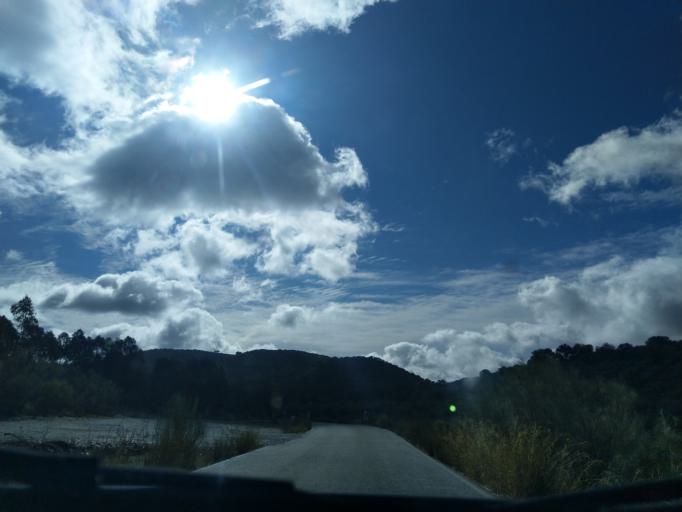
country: ES
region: Extremadura
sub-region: Provincia de Badajoz
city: Reina
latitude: 38.1271
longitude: -5.9144
